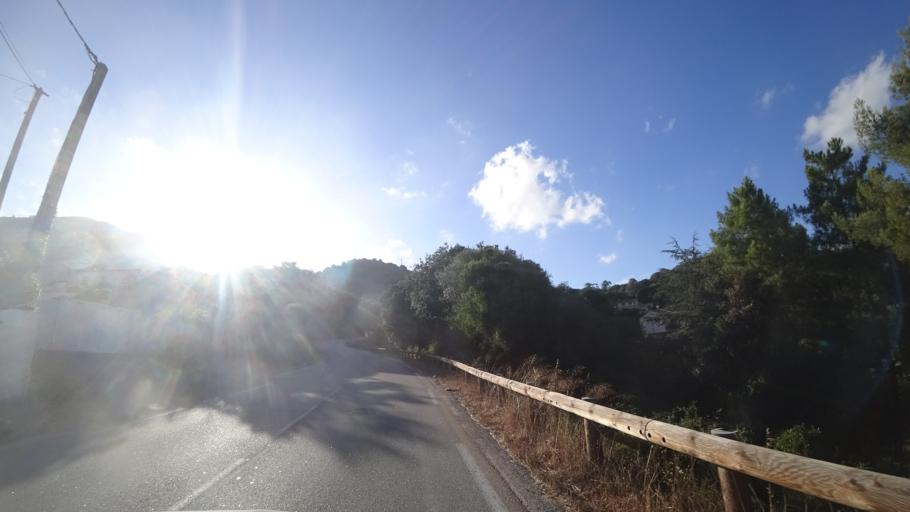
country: FR
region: Corsica
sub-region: Departement de la Corse-du-Sud
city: Alata
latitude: 41.9577
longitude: 8.7274
